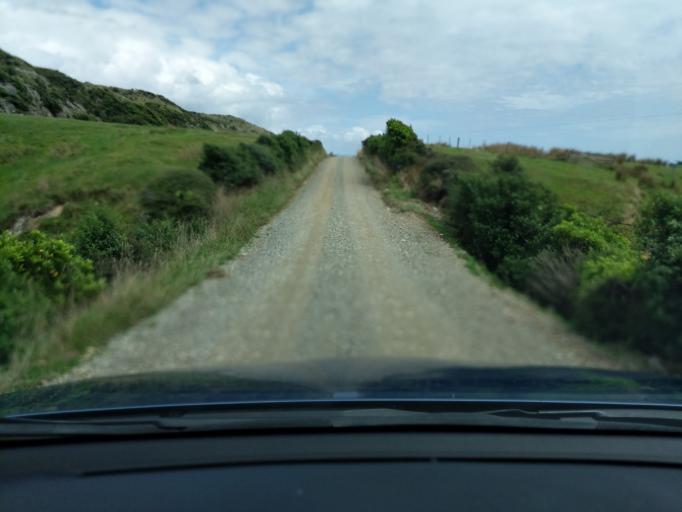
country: NZ
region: Tasman
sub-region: Tasman District
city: Takaka
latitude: -40.6639
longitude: 172.4097
